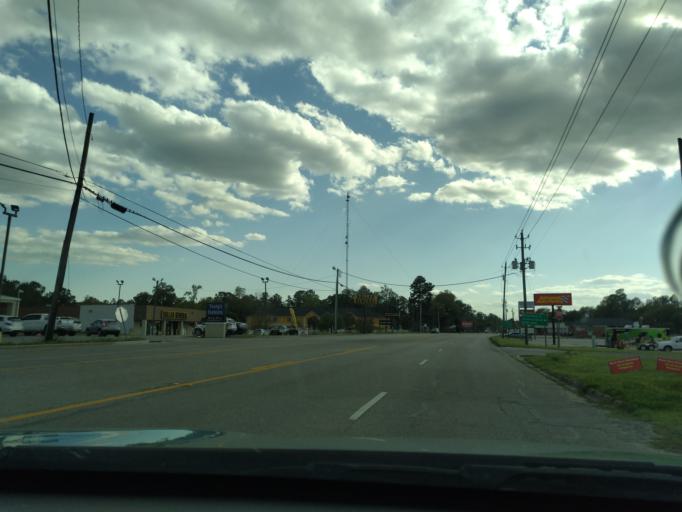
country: US
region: South Carolina
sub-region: Williamsburg County
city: Kingstree
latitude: 33.6848
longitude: -79.8226
